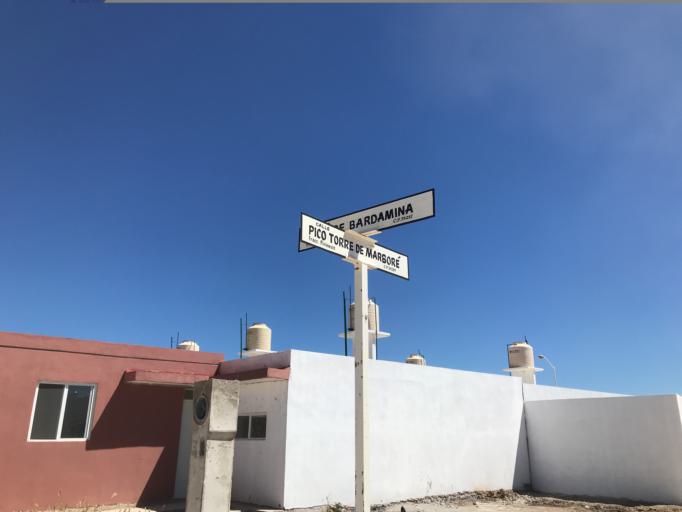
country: MX
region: Durango
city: Victoria de Durango
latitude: 24.0178
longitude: -104.5987
